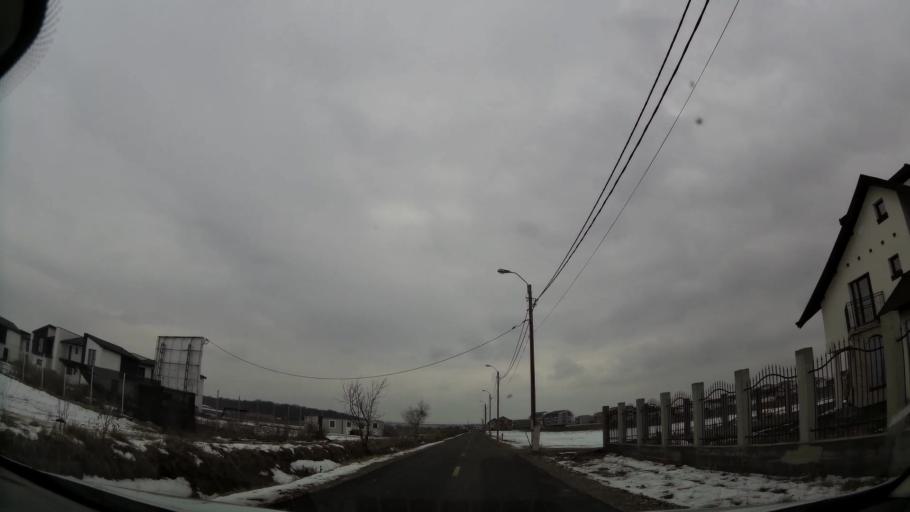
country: RO
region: Ilfov
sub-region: Comuna Otopeni
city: Otopeni
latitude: 44.5563
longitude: 26.1081
